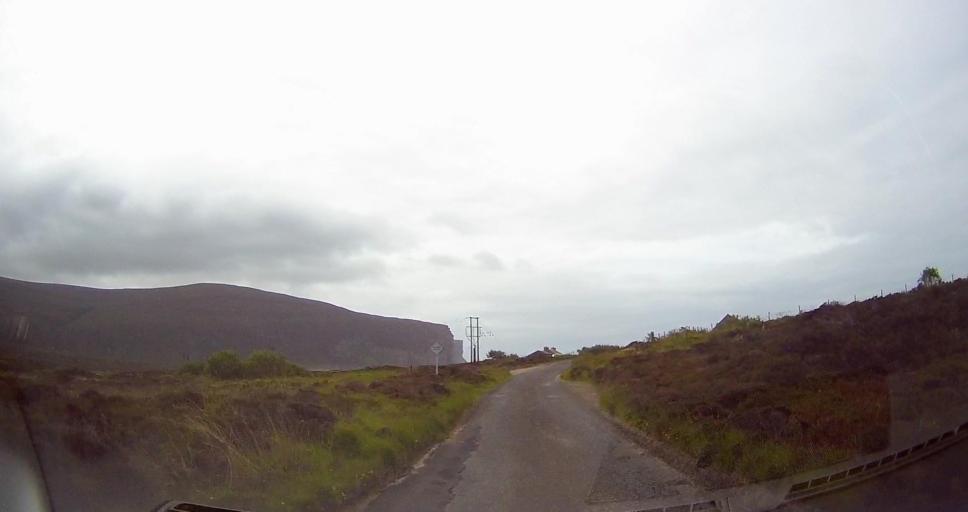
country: GB
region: Scotland
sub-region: Orkney Islands
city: Stromness
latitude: 58.8778
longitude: -3.3861
